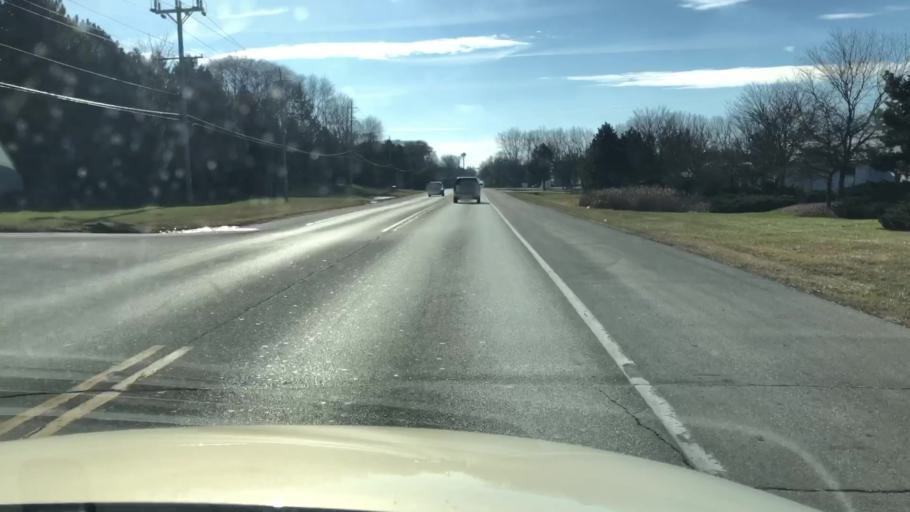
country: US
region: Wisconsin
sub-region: Waukesha County
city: Brookfield
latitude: 43.0513
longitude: -88.1666
